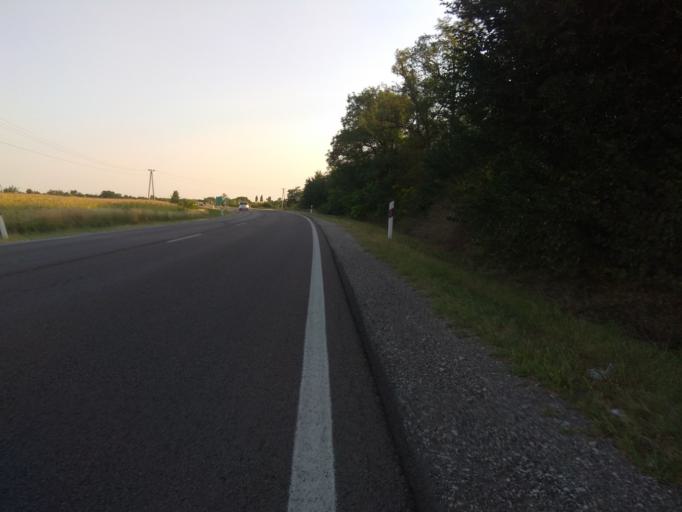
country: HU
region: Borsod-Abauj-Zemplen
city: Emod
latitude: 47.9458
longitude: 20.8312
